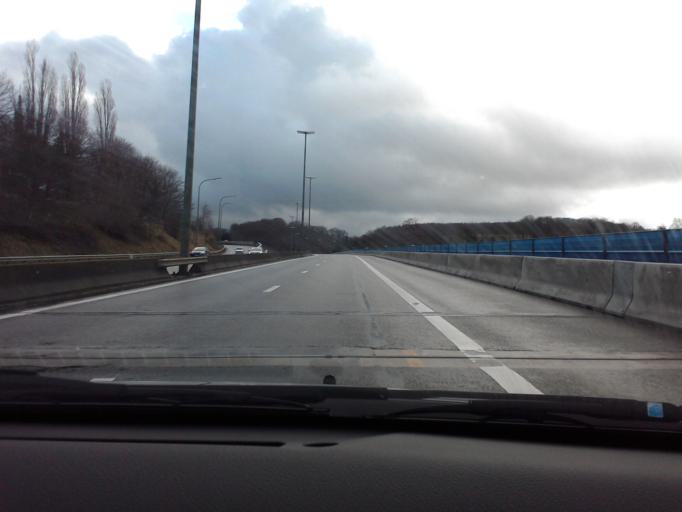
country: BE
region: Wallonia
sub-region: Province de Liege
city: Verviers
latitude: 50.5810
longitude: 5.8503
